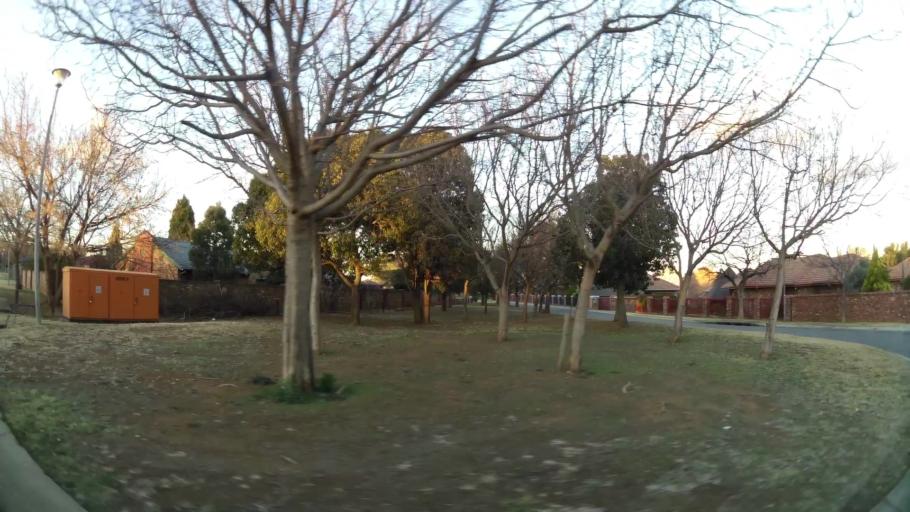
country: ZA
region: North-West
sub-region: Dr Kenneth Kaunda District Municipality
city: Potchefstroom
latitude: -26.7275
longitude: 27.1141
